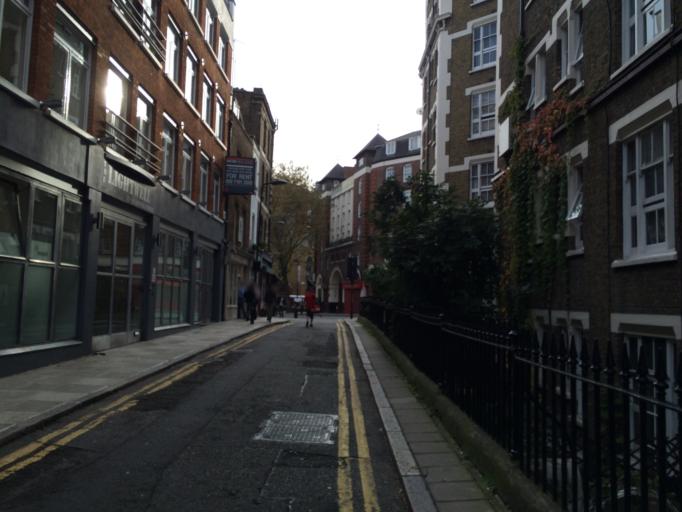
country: GB
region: England
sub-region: Greater London
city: Clerkenwell
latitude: 51.5223
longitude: -0.1116
